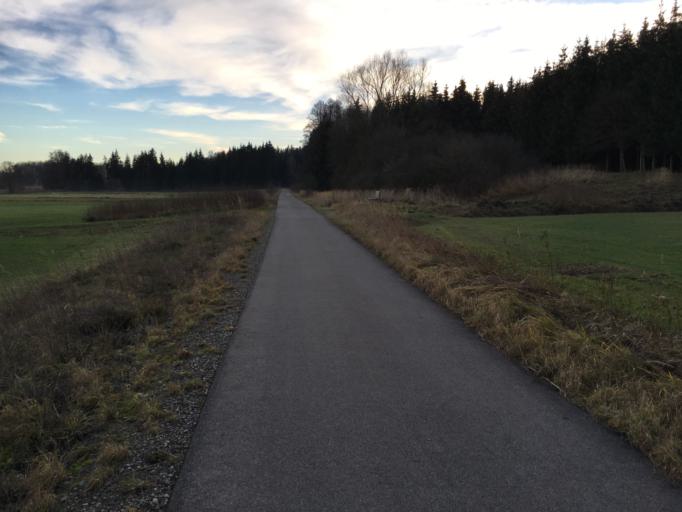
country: DE
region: Bavaria
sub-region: Swabia
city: Wald
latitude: 47.9902
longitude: 10.2863
